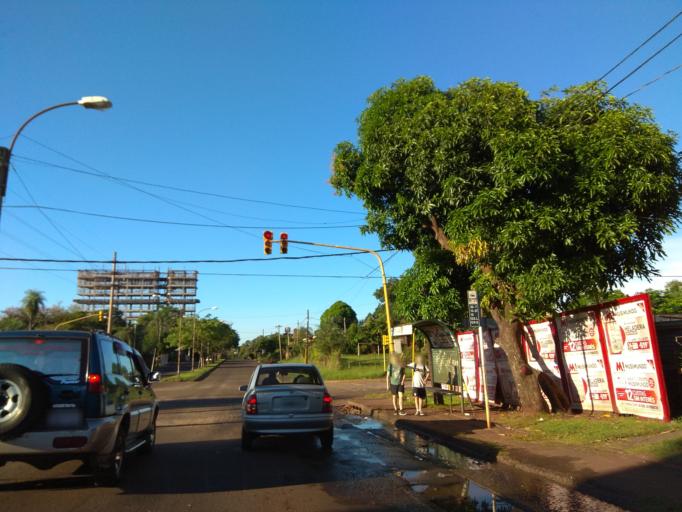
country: AR
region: Misiones
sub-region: Departamento de Capital
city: Posadas
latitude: -27.3915
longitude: -55.8934
